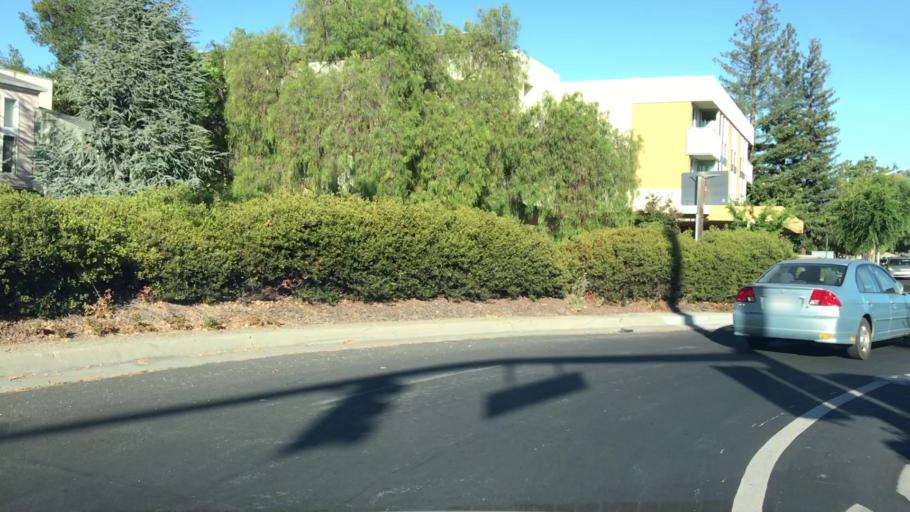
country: US
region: California
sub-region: Santa Clara County
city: Palo Alto
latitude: 37.4158
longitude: -122.1278
